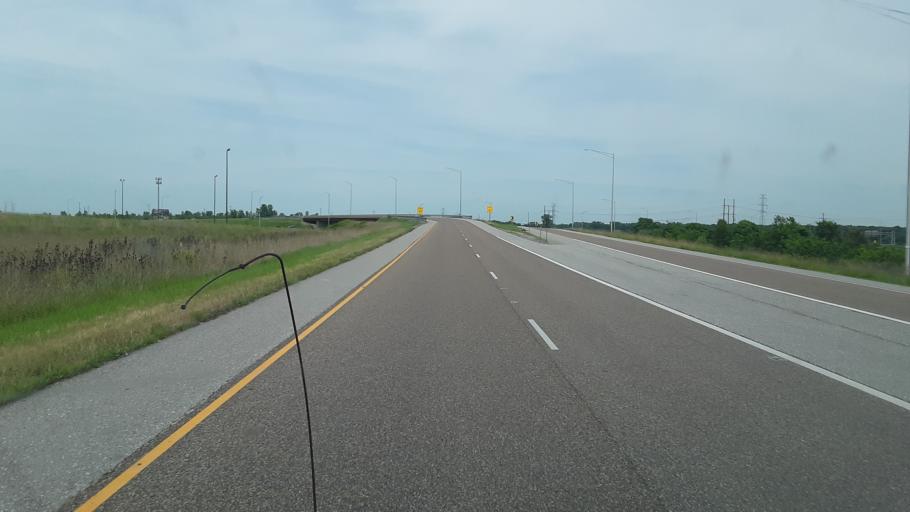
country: US
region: Illinois
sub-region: Madison County
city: Mitchell
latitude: 38.7540
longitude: -90.0419
